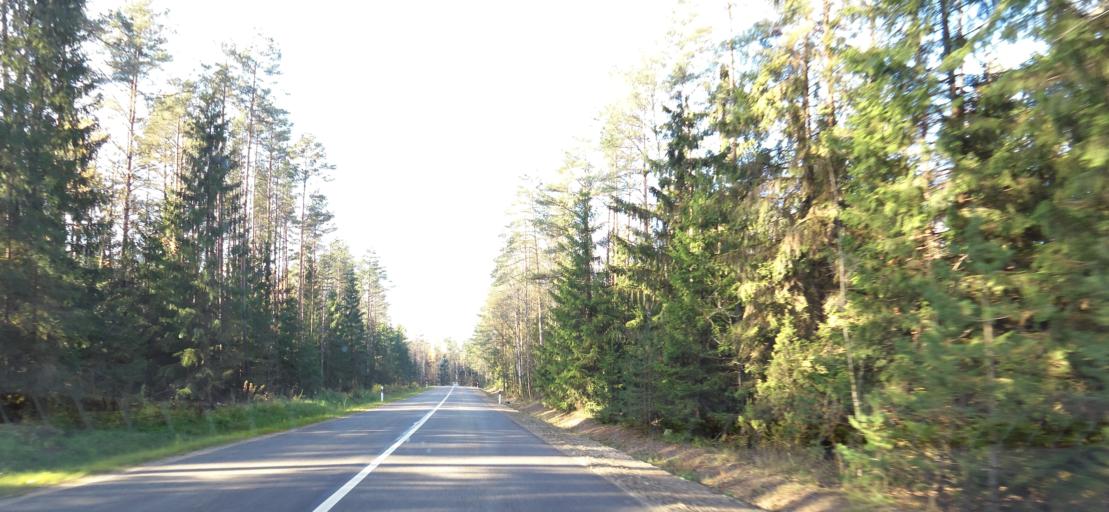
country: LT
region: Vilnius County
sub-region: Trakai
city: Rudiskes
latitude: 54.5095
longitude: 24.8862
